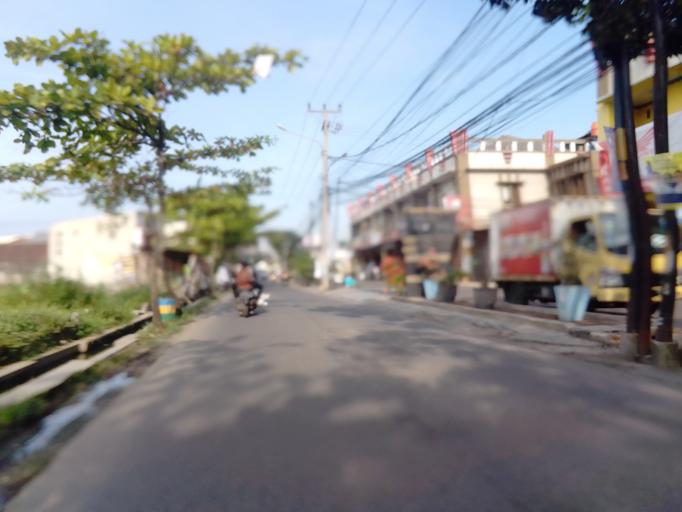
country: ID
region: West Java
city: Cileunyi
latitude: -6.9241
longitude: 107.7013
